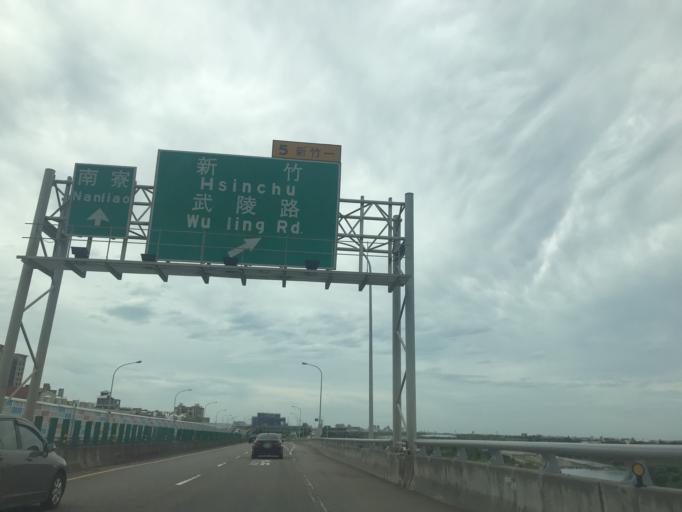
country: TW
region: Taiwan
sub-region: Hsinchu
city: Hsinchu
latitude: 24.8250
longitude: 120.9770
